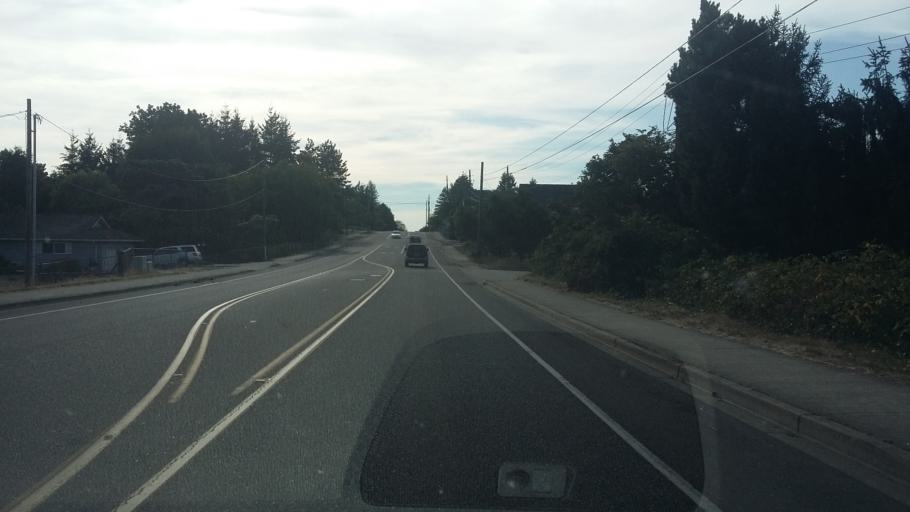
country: US
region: Washington
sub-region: Clark County
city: Walnut Grove
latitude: 45.6681
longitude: -122.5820
